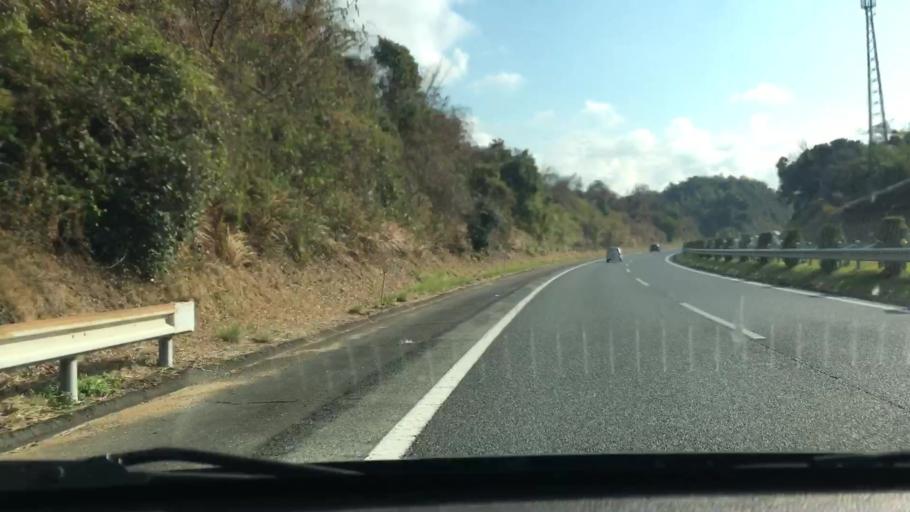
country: JP
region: Kumamoto
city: Matsubase
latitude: 32.6370
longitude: 130.7095
